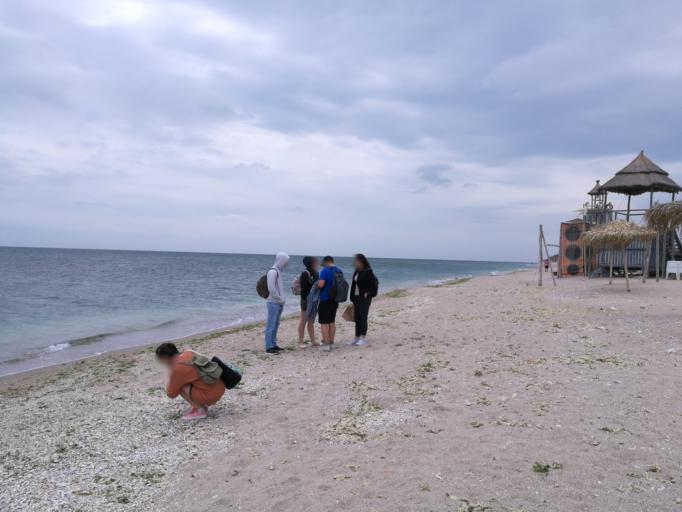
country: RO
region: Constanta
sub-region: Municipiul Mangalia
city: Mangalia
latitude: 43.7509
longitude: 28.5771
